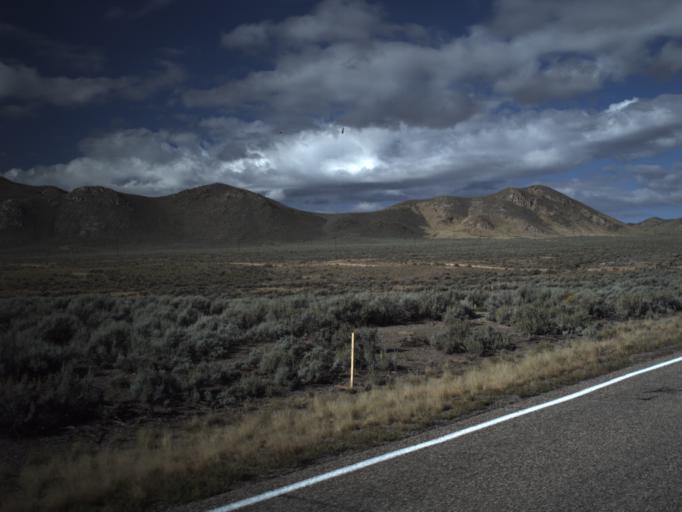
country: US
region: Utah
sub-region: Beaver County
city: Milford
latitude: 38.4161
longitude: -113.0833
